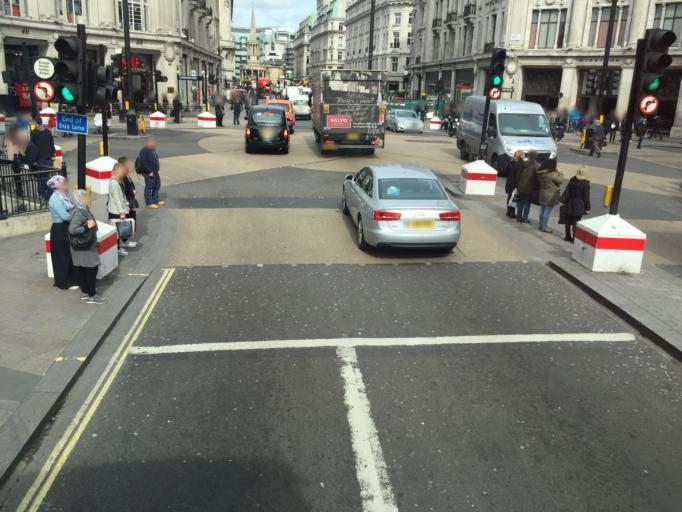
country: GB
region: England
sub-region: Greater London
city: London
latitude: 51.5150
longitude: -0.1421
